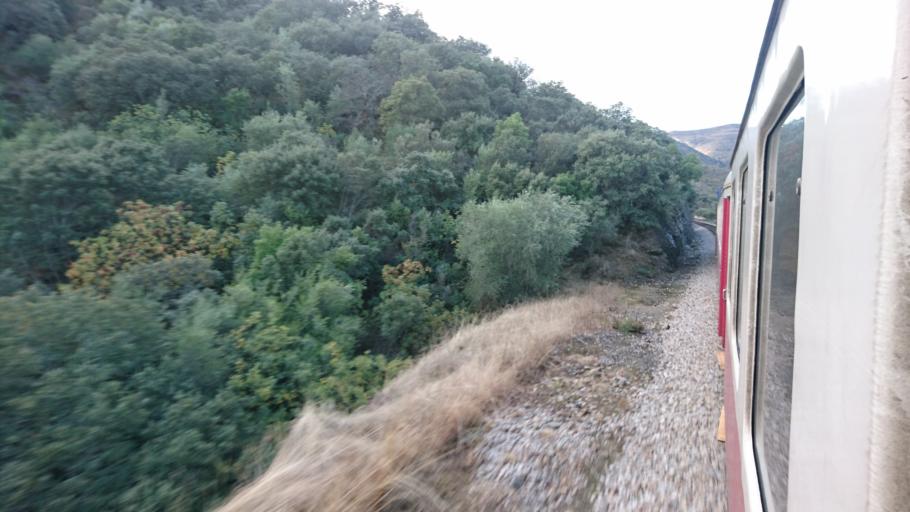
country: PT
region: Guarda
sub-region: Vila Nova de Foz Coa
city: Vila Nova de Foz Coa
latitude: 41.1286
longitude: -7.1563
